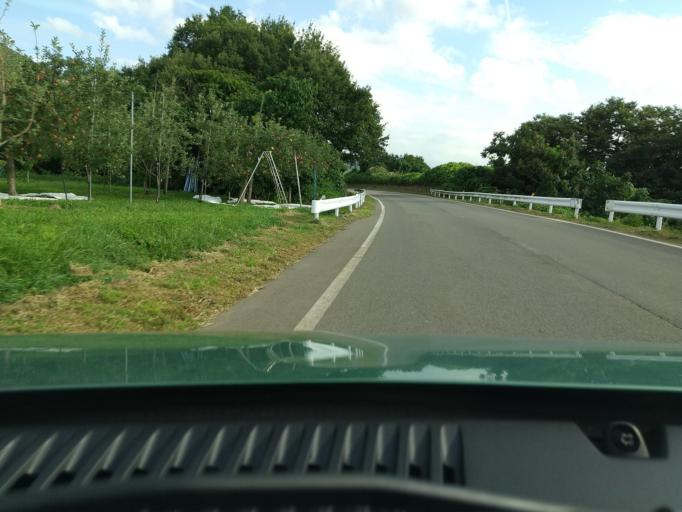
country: JP
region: Akita
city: Yuzawa
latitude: 39.2221
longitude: 140.5657
